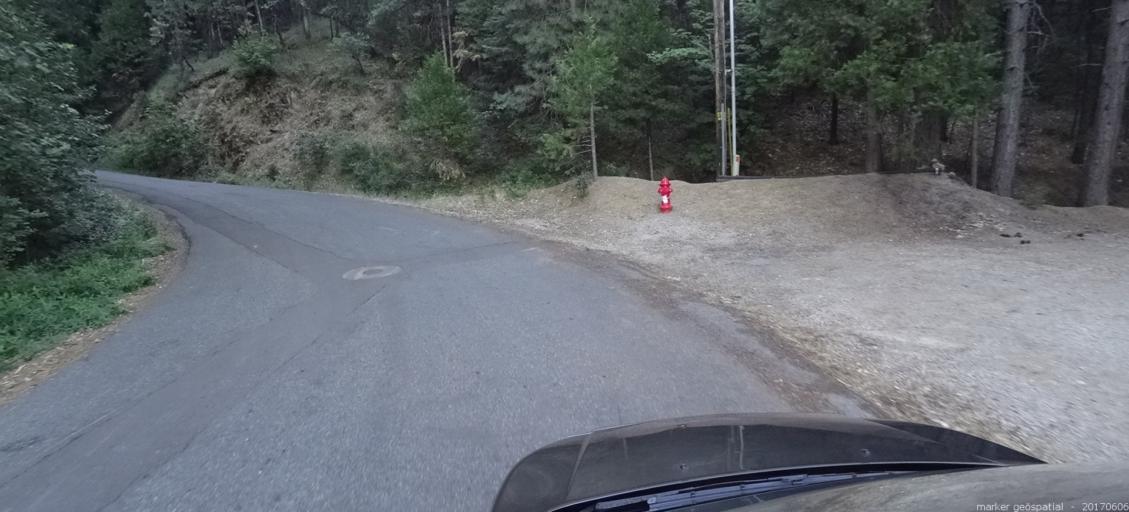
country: US
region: California
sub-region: Siskiyou County
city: Dunsmuir
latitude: 41.1993
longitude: -122.2709
